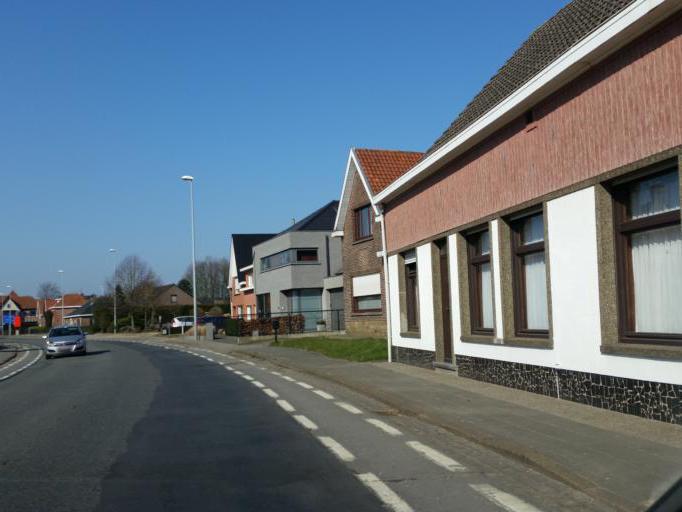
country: BE
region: Flanders
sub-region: Provincie Oost-Vlaanderen
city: Wachtebeke
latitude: 51.1666
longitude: 3.8610
